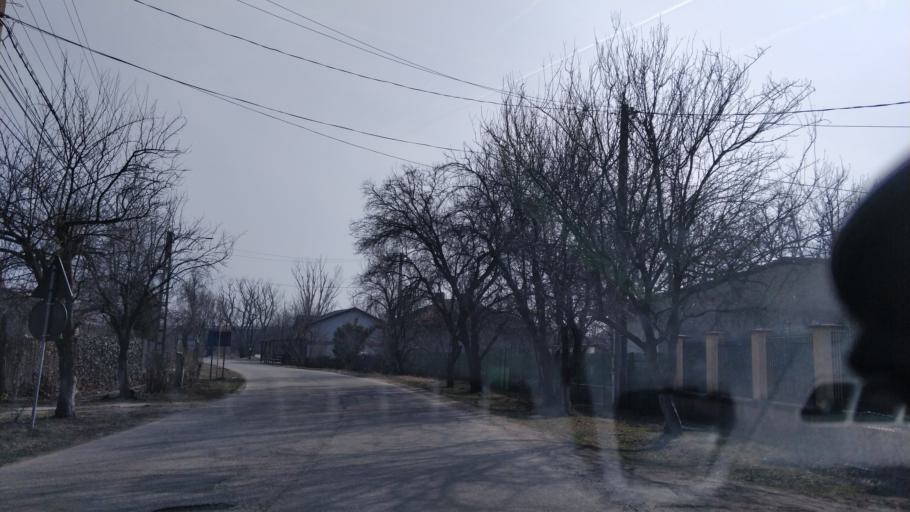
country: RO
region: Giurgiu
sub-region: Comuna Ulmi
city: Ulmi
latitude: 44.4697
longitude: 25.7677
